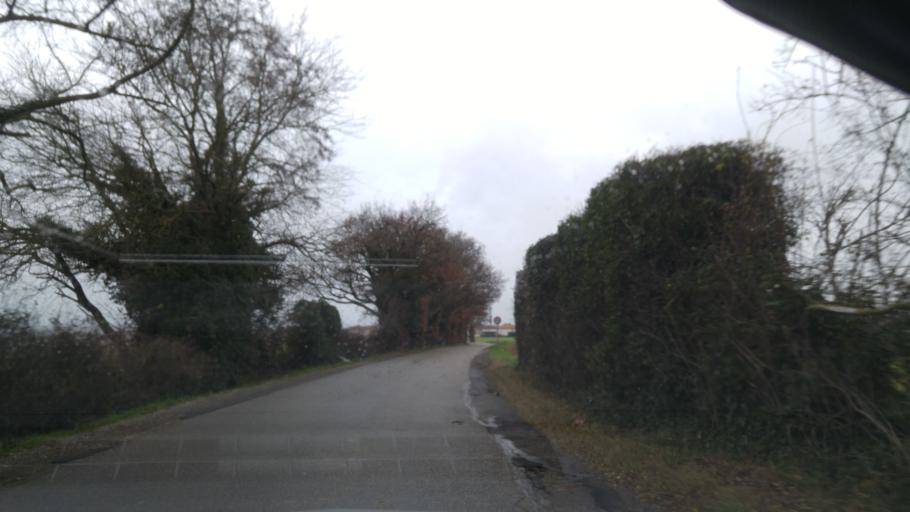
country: FR
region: Rhone-Alpes
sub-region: Departement du Rhone
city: Saint-Laurent-de-Mure
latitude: 45.6977
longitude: 5.0401
